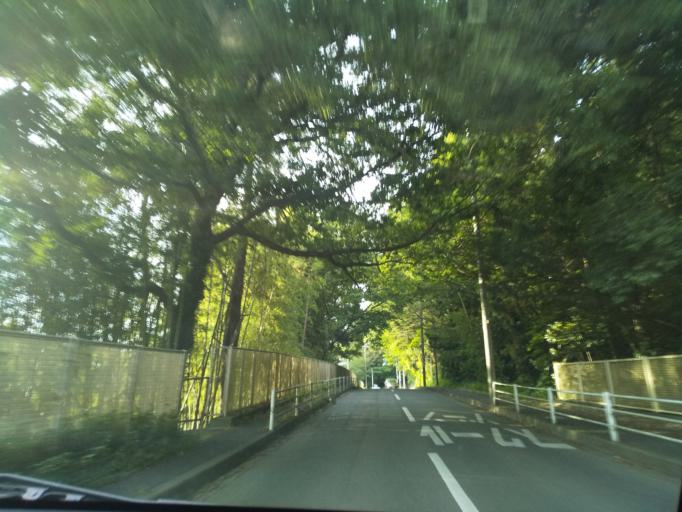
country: JP
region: Kanagawa
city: Zama
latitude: 35.5179
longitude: 139.3854
